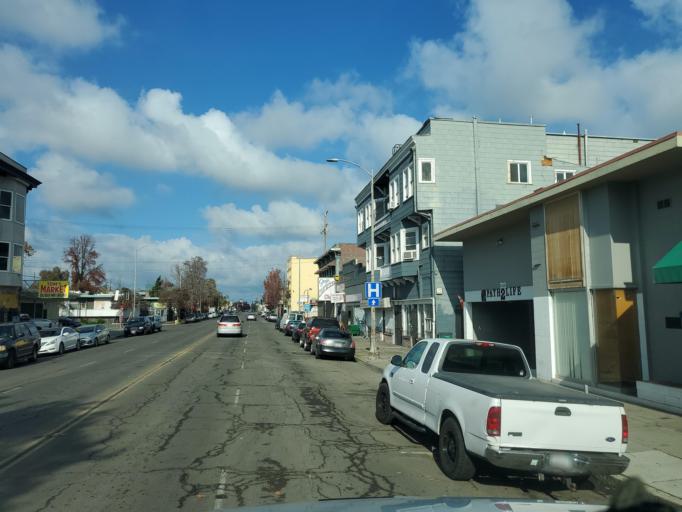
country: US
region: California
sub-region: San Joaquin County
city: Stockton
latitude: 37.9570
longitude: -121.2855
